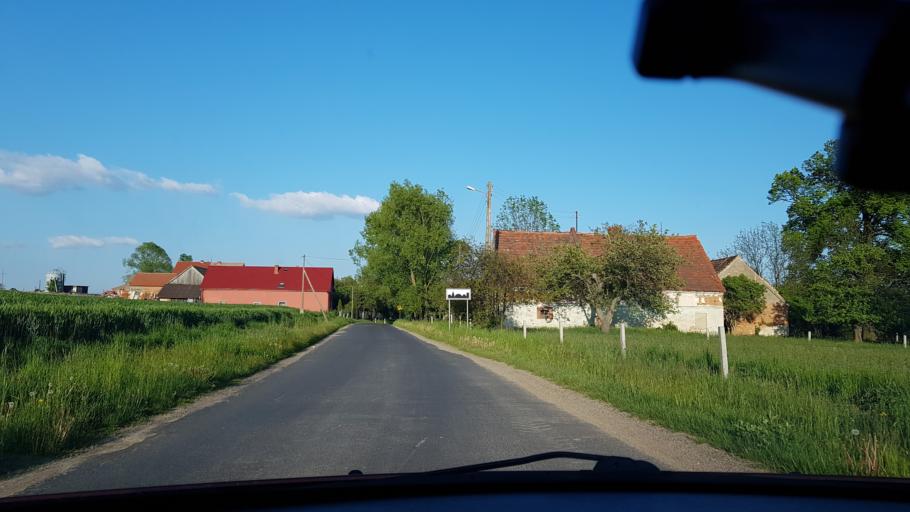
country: PL
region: Lower Silesian Voivodeship
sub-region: Powiat zabkowicki
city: Budzow
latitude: 50.6106
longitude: 16.7041
